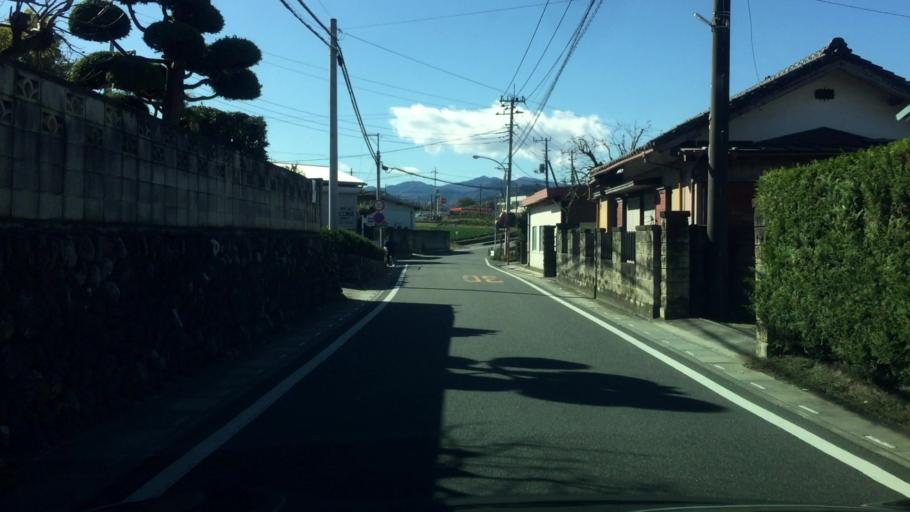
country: JP
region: Saitama
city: Kodamacho-kodamaminami
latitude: 36.1840
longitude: 139.1262
